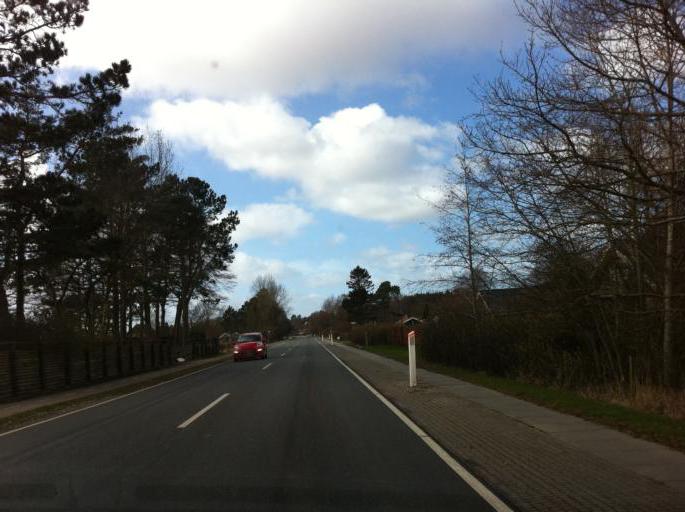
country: DK
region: Central Jutland
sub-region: Syddjurs Kommune
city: Ebeltoft
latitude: 56.2280
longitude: 10.6261
